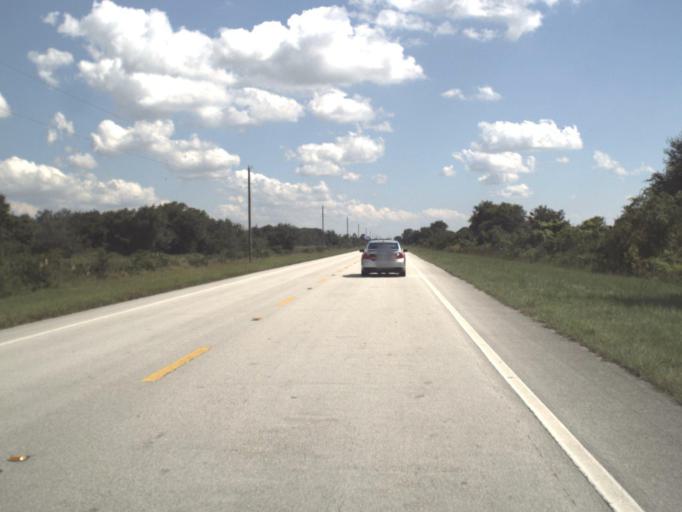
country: US
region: Florida
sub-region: Highlands County
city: Lake Placid
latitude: 27.3924
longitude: -81.1490
